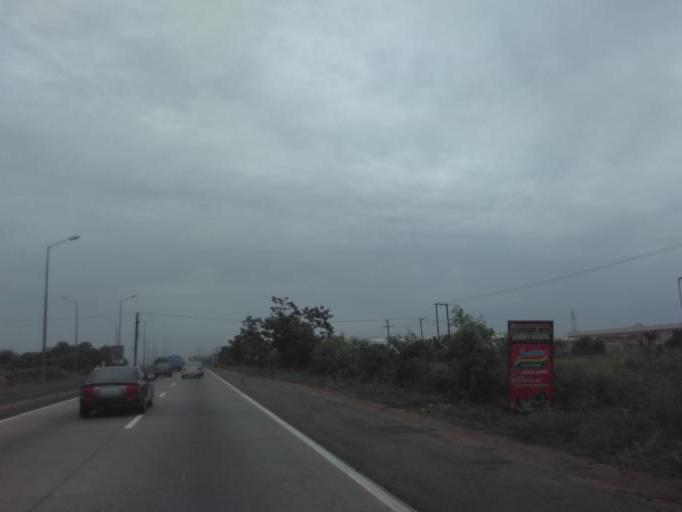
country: GH
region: Greater Accra
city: Medina Estates
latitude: 5.6297
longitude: -0.1556
